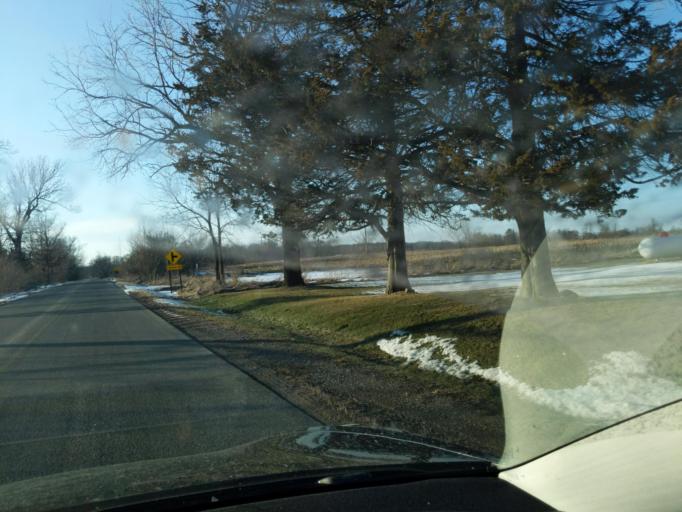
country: US
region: Michigan
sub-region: Ingham County
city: Stockbridge
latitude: 42.5246
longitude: -84.2560
